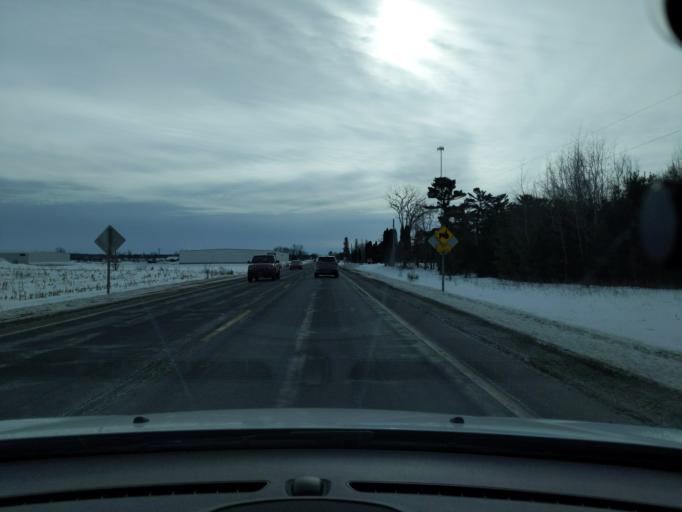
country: US
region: Wisconsin
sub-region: Barron County
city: Turtle Lake
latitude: 45.3928
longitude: -92.1665
